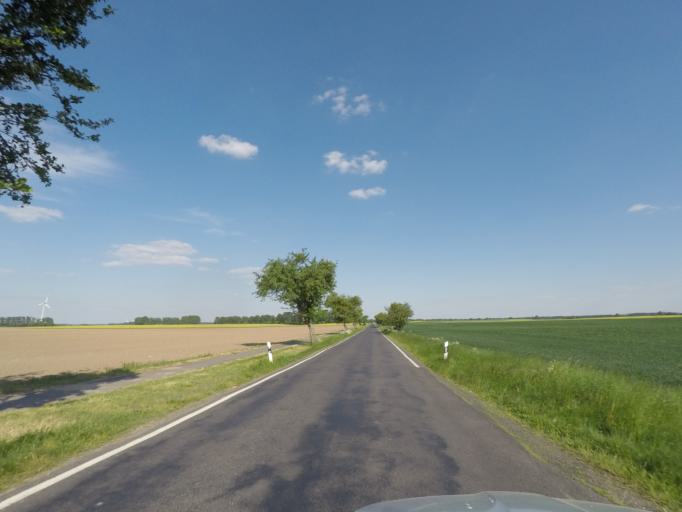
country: DE
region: Brandenburg
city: Werftpfuhl
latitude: 52.7349
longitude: 13.8487
